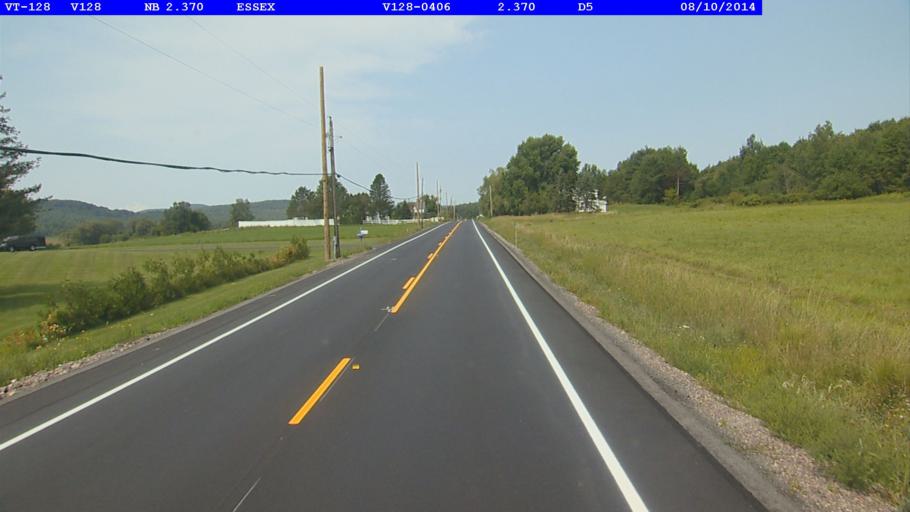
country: US
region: Vermont
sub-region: Chittenden County
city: Jericho
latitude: 44.5319
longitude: -73.0311
